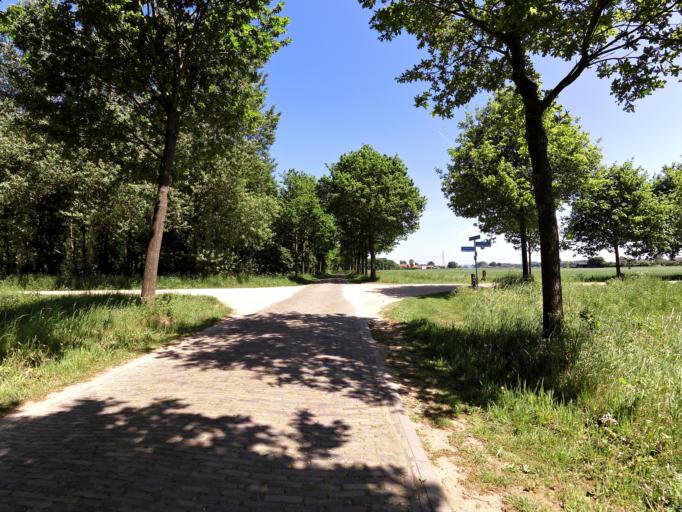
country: NL
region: Gelderland
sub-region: Gemeente Bronckhorst
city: Baak
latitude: 52.0640
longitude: 6.2413
